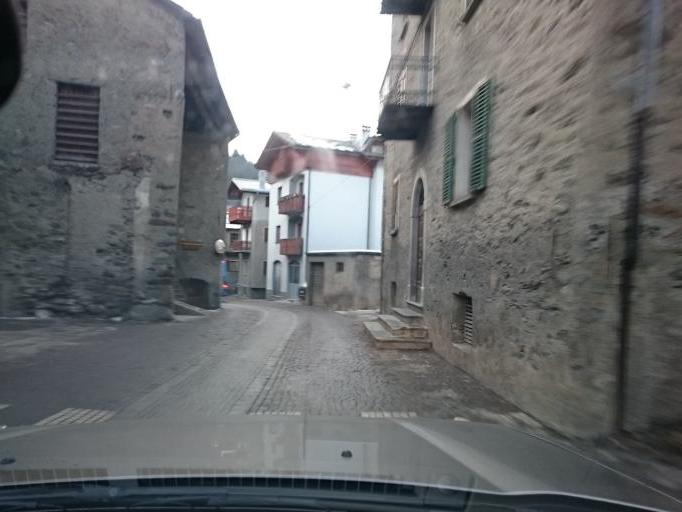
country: IT
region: Lombardy
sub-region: Provincia di Sondrio
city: Sant'Antonio
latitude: 46.4584
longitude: 10.4252
